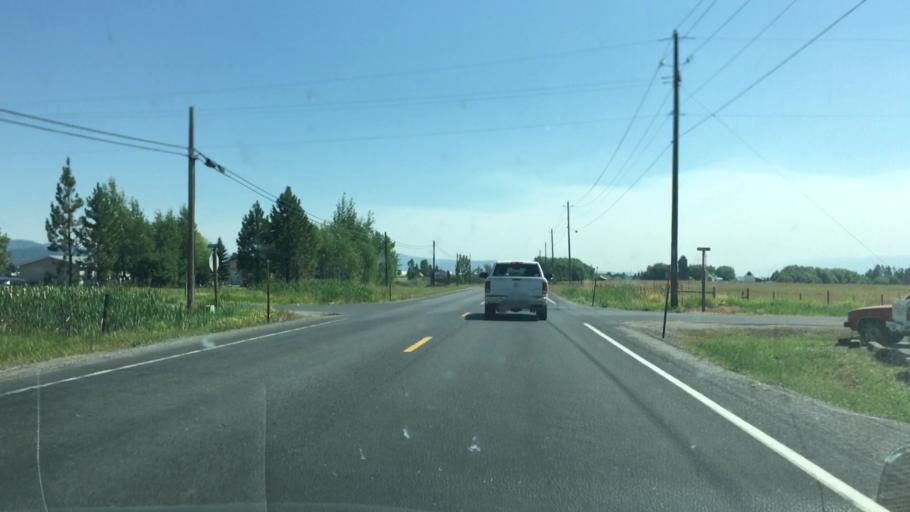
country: US
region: Idaho
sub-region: Valley County
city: McCall
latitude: 44.8473
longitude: -116.0896
